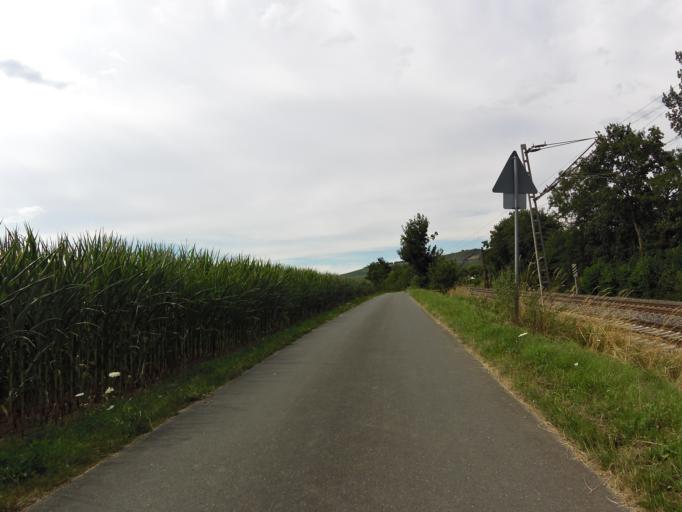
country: DE
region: Bavaria
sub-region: Regierungsbezirk Unterfranken
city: Randersacker
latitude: 49.7473
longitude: 9.9793
